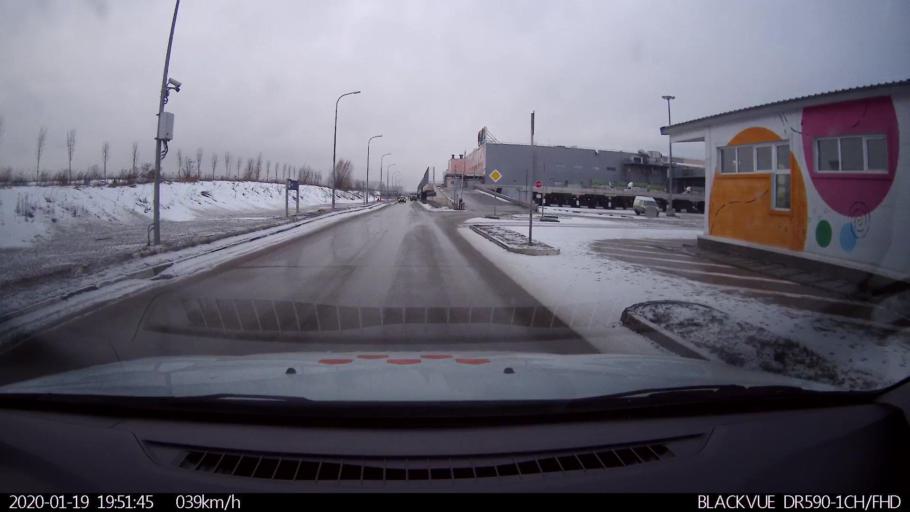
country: RU
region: Nizjnij Novgorod
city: Afonino
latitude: 56.2229
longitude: 44.0696
